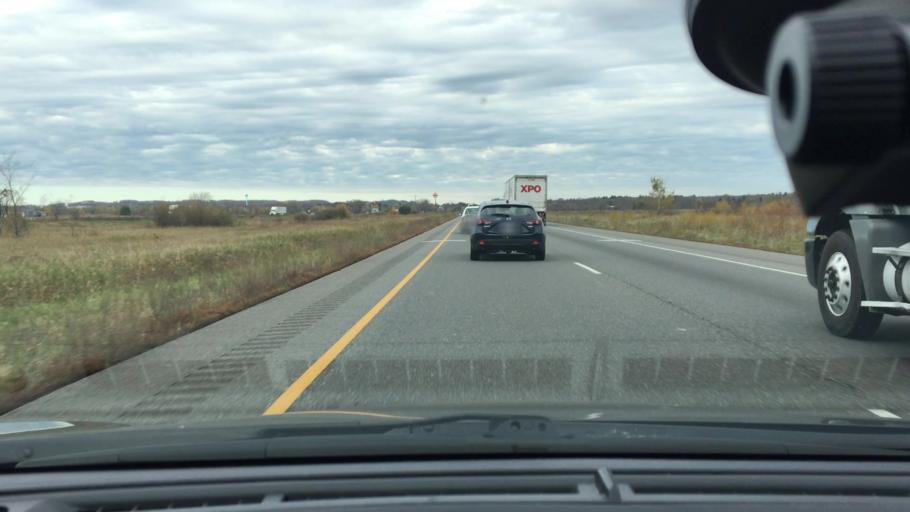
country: US
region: Wisconsin
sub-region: Monroe County
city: Tomah
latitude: 43.9552
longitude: -90.3502
